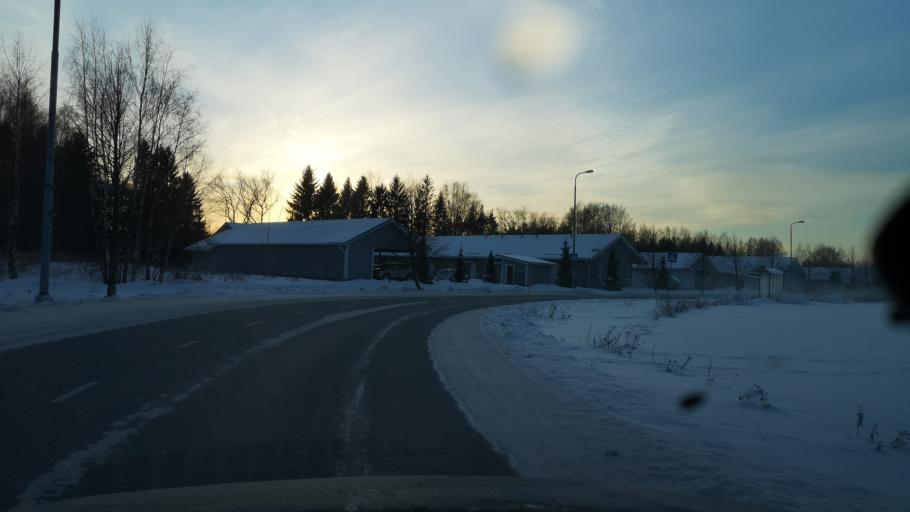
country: FI
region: Satakunta
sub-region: Pori
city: Pori
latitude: 61.5025
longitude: 21.8353
